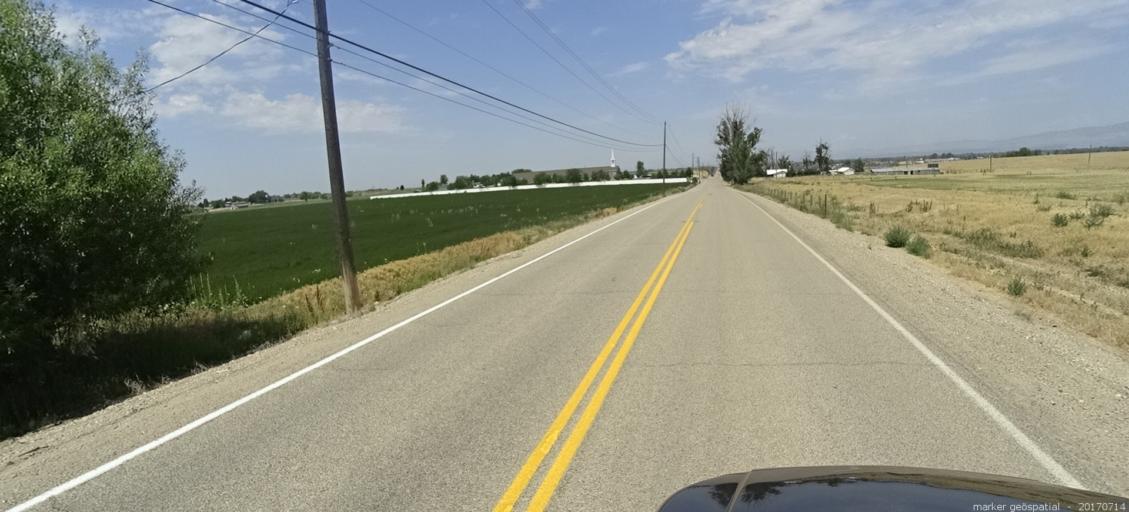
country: US
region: Idaho
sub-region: Ada County
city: Meridian
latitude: 43.5411
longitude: -116.3543
